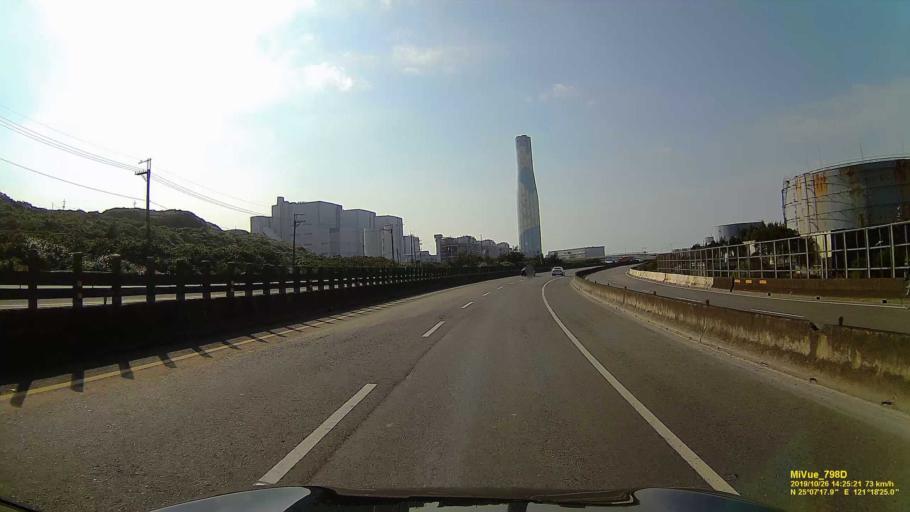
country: TW
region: Taiwan
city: Taoyuan City
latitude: 25.1218
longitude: 121.3061
